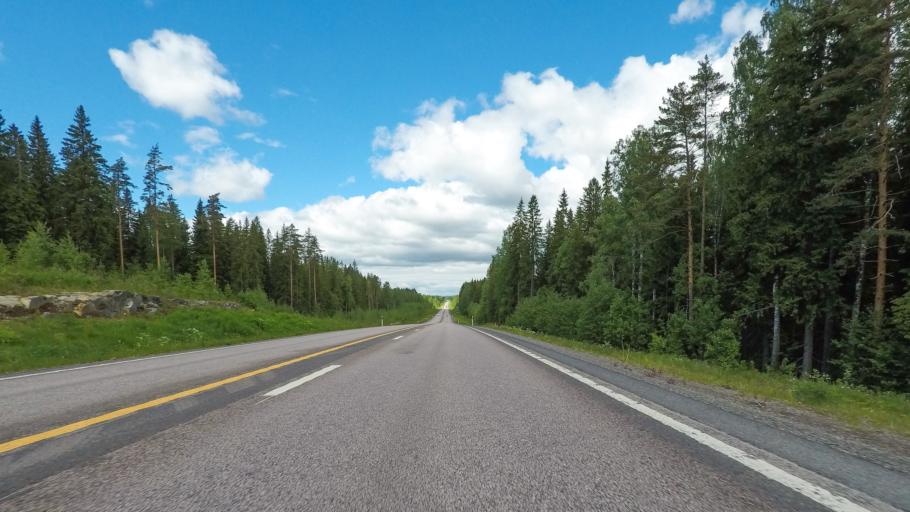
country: FI
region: Paijanne Tavastia
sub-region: Lahti
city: Heinola
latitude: 61.3893
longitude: 26.0522
